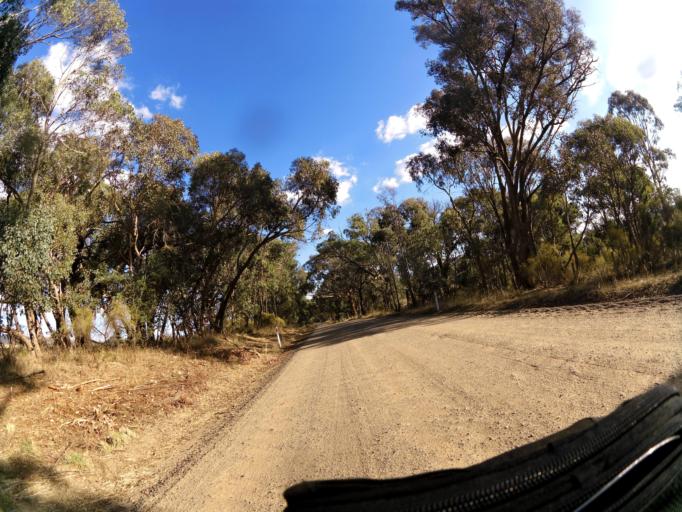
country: AU
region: Victoria
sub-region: Greater Bendigo
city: Kennington
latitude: -37.0221
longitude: 144.8006
